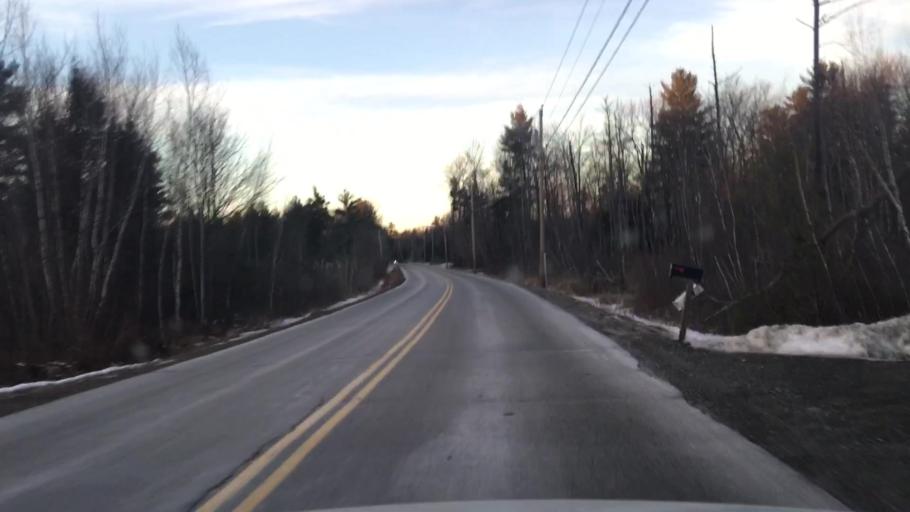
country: US
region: Maine
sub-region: York County
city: Lebanon
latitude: 43.3517
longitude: -70.8674
